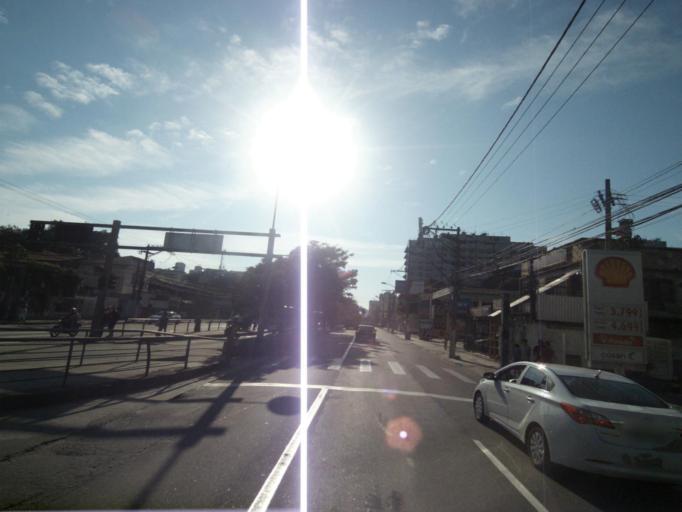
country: BR
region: Rio de Janeiro
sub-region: Niteroi
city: Niteroi
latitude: -22.8808
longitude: -43.1038
